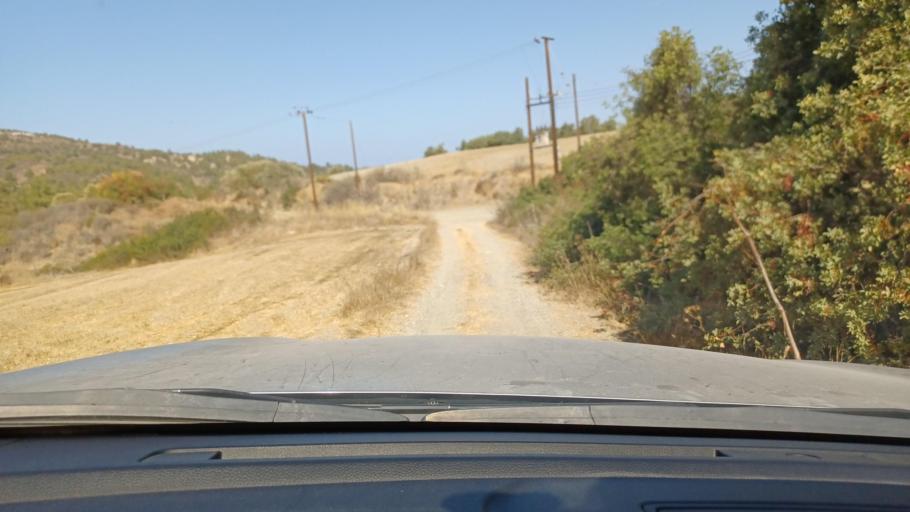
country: CY
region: Pafos
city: Polis
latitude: 35.0000
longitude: 32.4997
